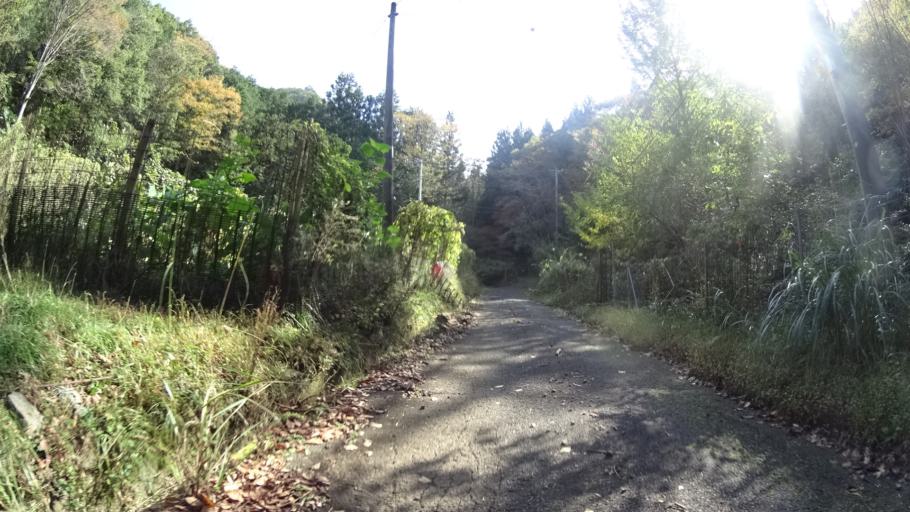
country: JP
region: Yamanashi
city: Otsuki
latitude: 35.5815
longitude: 138.9746
